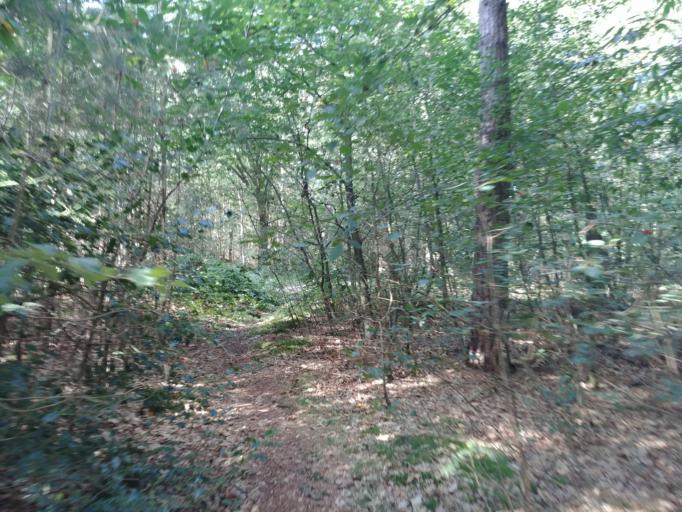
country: NL
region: Utrecht
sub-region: Gemeente Utrechtse Heuvelrug
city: Doorn
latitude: 52.0440
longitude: 5.3573
